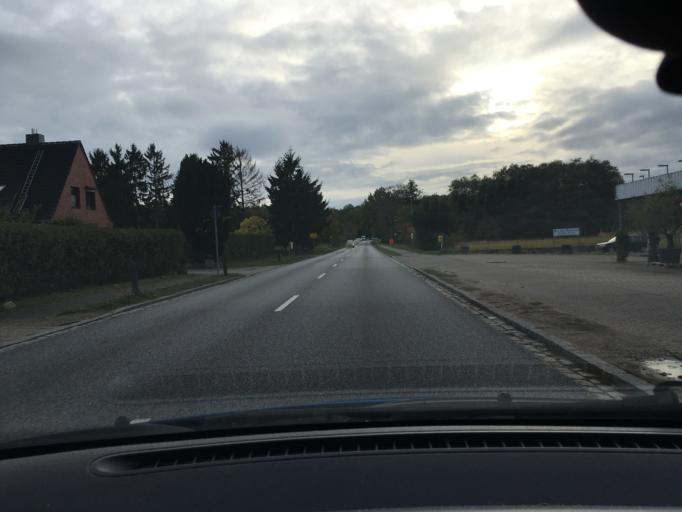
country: DE
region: Schleswig-Holstein
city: Elmenhorst
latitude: 53.5429
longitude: 10.5353
